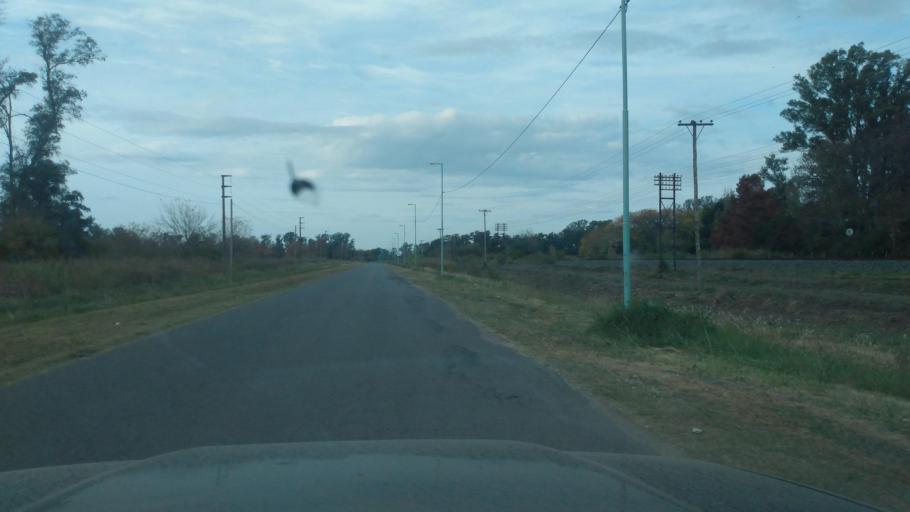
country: AR
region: Buenos Aires
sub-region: Partido de Lujan
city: Lujan
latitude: -34.5990
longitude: -59.1694
